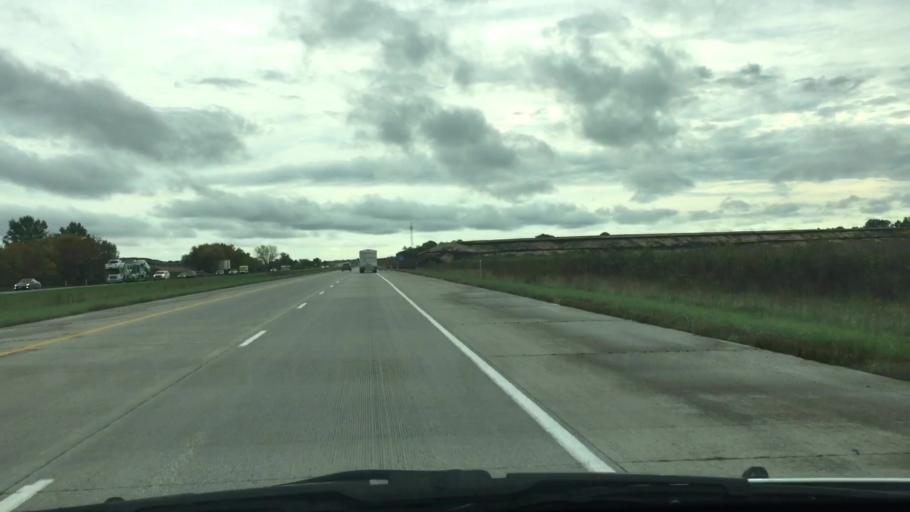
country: US
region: Iowa
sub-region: Polk County
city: West Des Moines
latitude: 41.5033
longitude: -93.7806
